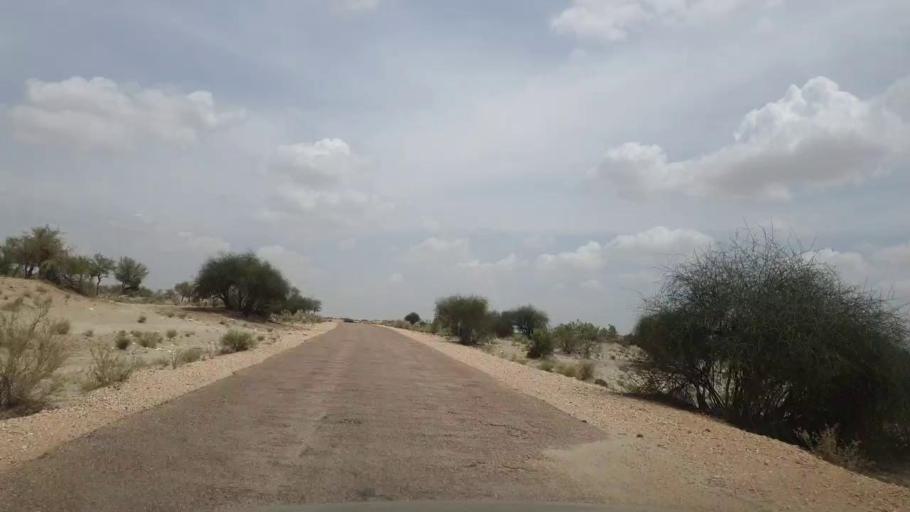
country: PK
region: Sindh
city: Kot Diji
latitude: 27.1790
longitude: 69.1864
